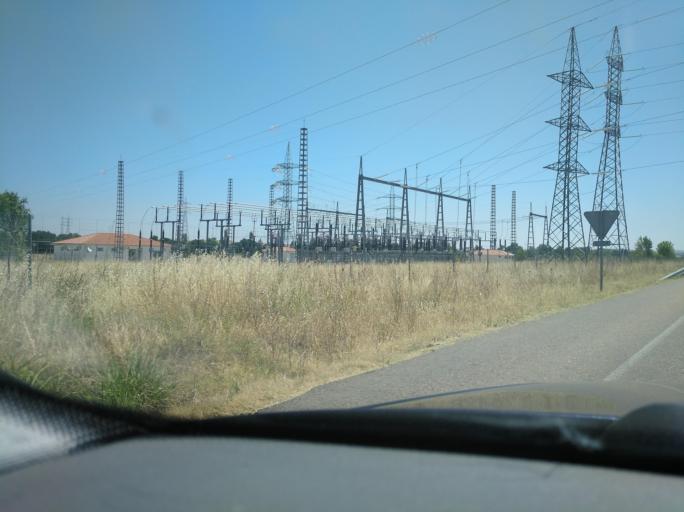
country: ES
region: Extremadura
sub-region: Provincia de Badajoz
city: Olivenza
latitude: 38.7384
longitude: -7.0641
